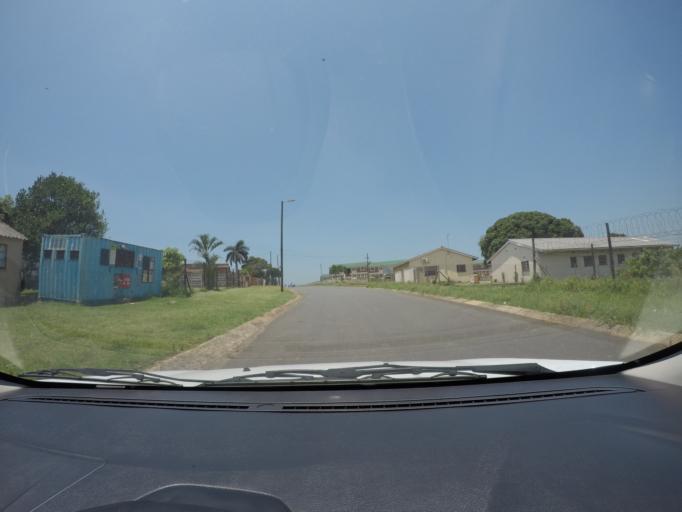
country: ZA
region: KwaZulu-Natal
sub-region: uThungulu District Municipality
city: eSikhawini
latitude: -28.8764
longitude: 31.9040
